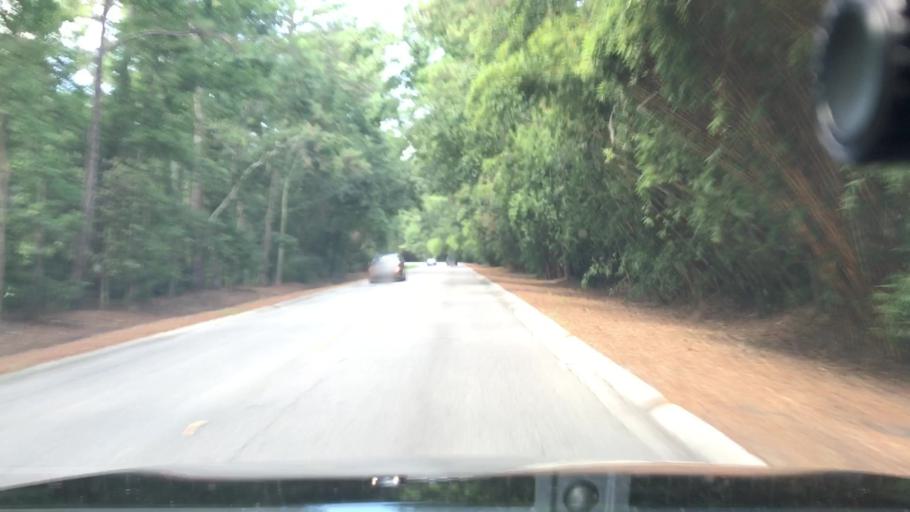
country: US
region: South Carolina
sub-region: Beaufort County
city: Hilton Head Island
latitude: 32.1499
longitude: -80.7775
